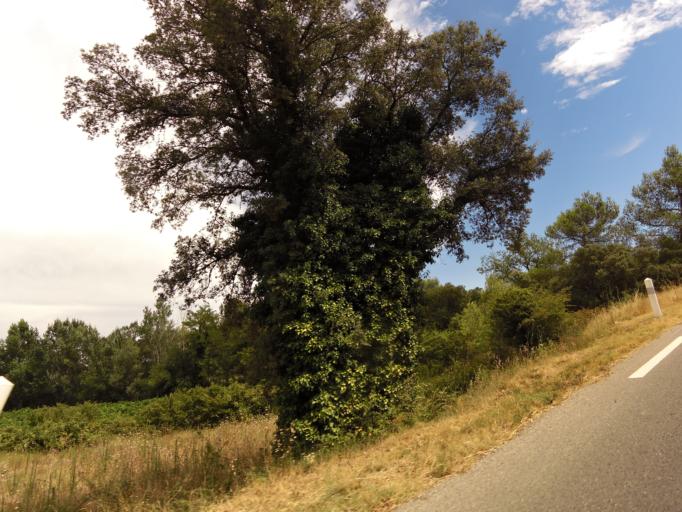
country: FR
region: Languedoc-Roussillon
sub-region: Departement du Gard
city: Sommieres
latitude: 43.8259
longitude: 4.0494
